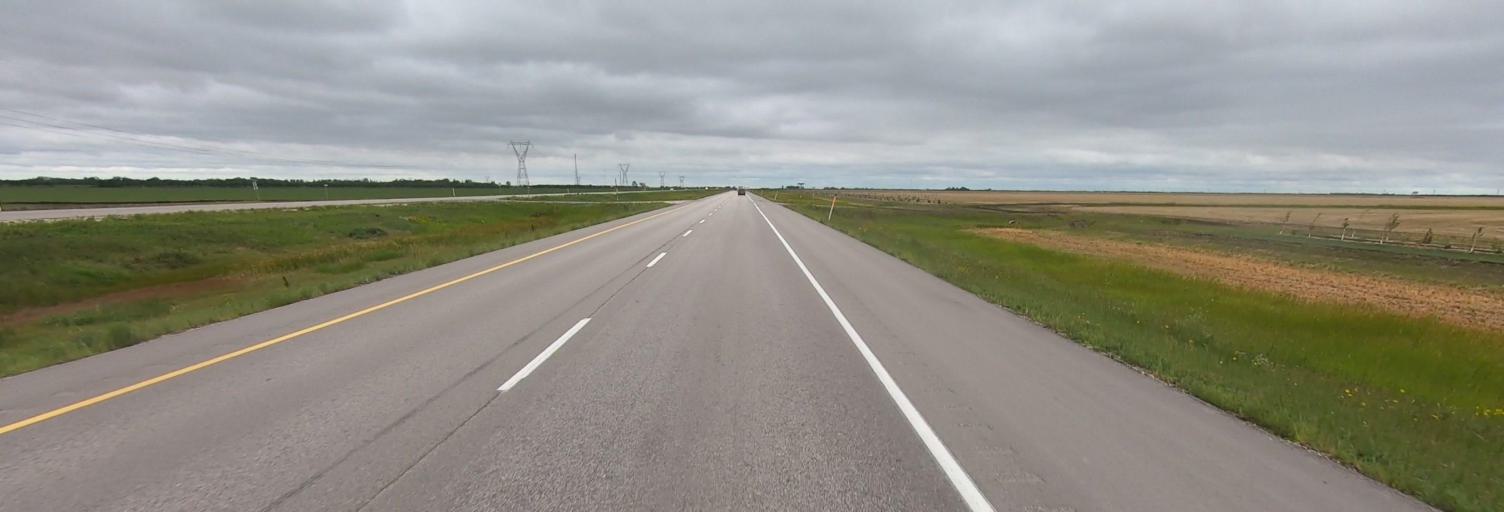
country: CA
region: Manitoba
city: Headingley
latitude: 49.8871
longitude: -97.6169
